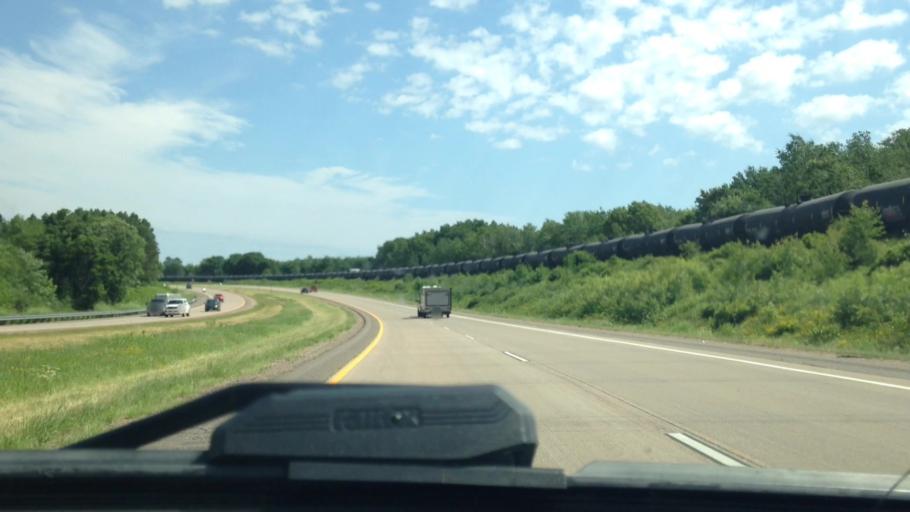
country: US
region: Wisconsin
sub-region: Washburn County
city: Spooner
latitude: 45.8650
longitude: -91.8341
